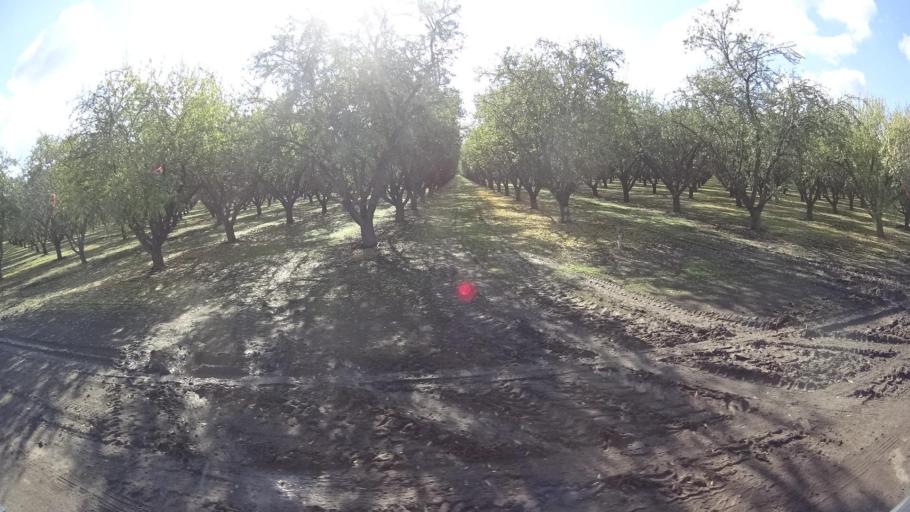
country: US
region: California
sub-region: Kern County
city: McFarland
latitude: 35.6527
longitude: -119.2341
